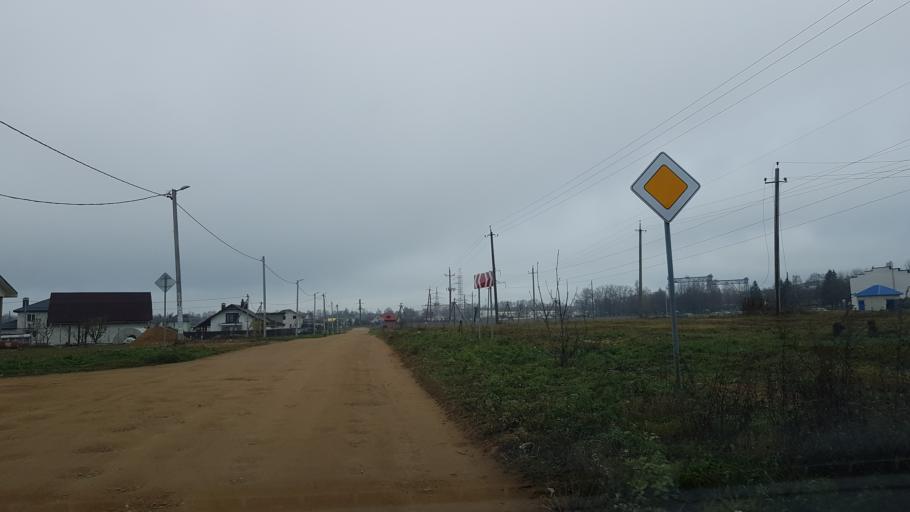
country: BY
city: Fanipol
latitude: 53.7314
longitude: 27.3293
